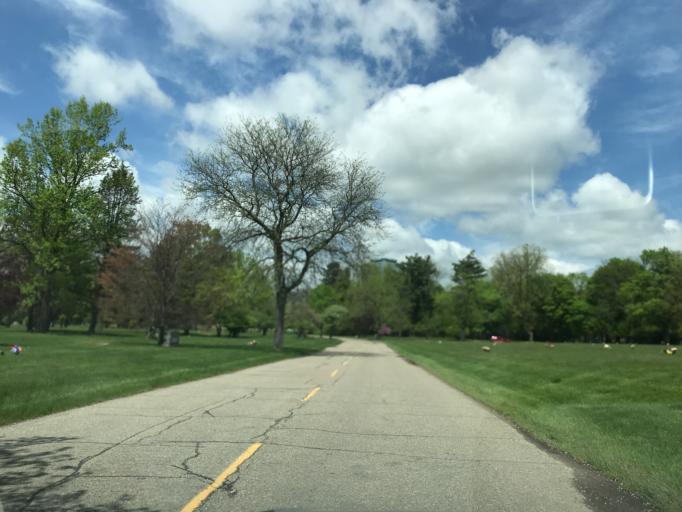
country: US
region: Michigan
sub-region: Oakland County
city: Franklin
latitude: 42.4829
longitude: -83.2999
